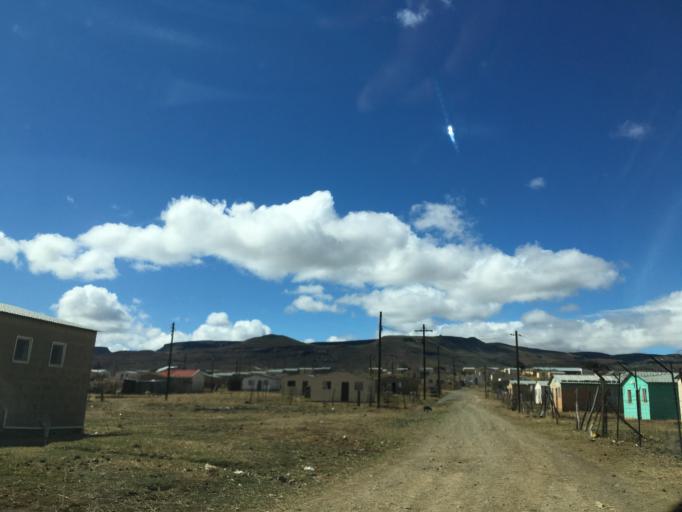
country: ZA
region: Eastern Cape
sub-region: Chris Hani District Municipality
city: Cala
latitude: -31.5401
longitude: 27.6783
